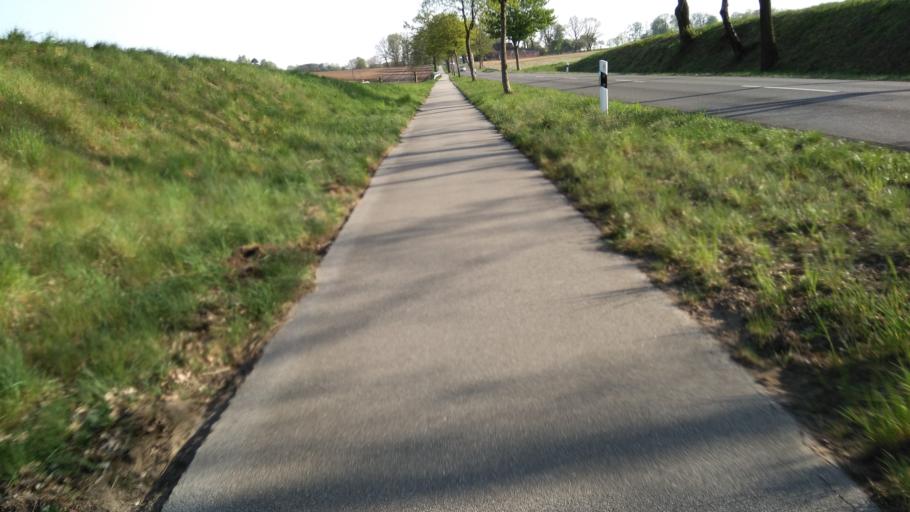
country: DE
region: Lower Saxony
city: Apensen
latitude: 53.4347
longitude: 9.6570
